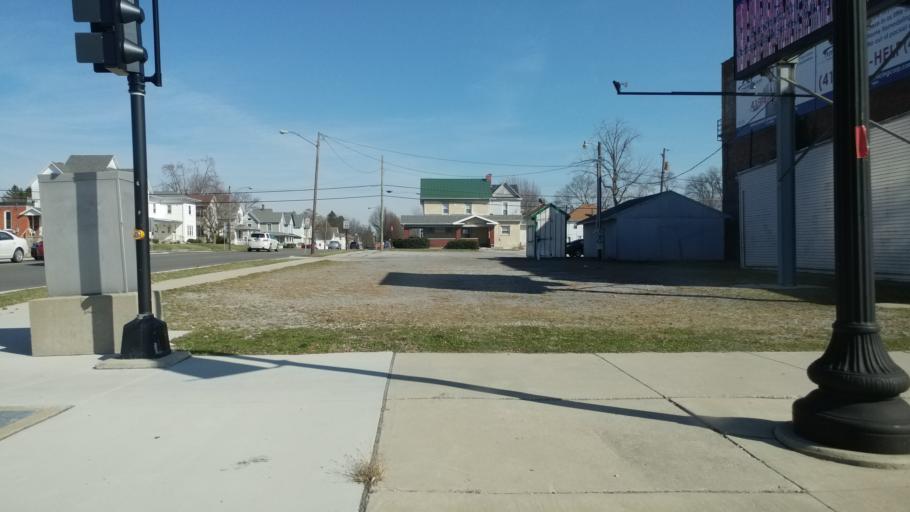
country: US
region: Ohio
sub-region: Hancock County
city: Findlay
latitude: 41.0439
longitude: -83.6500
